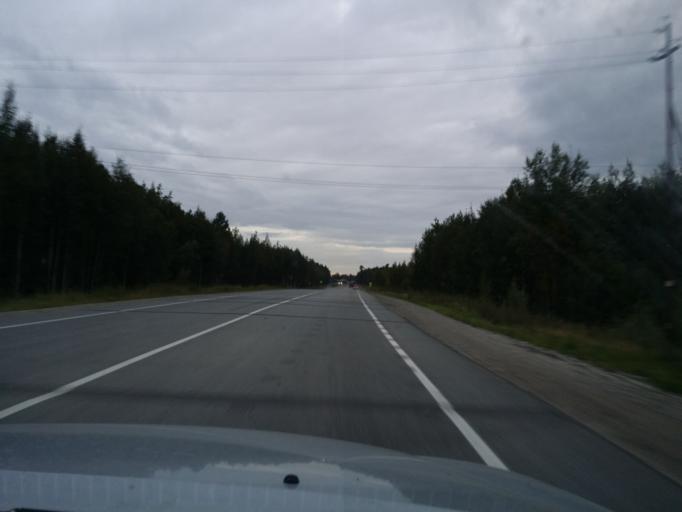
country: RU
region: Khanty-Mansiyskiy Avtonomnyy Okrug
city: Izluchinsk
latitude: 61.0139
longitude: 76.7910
